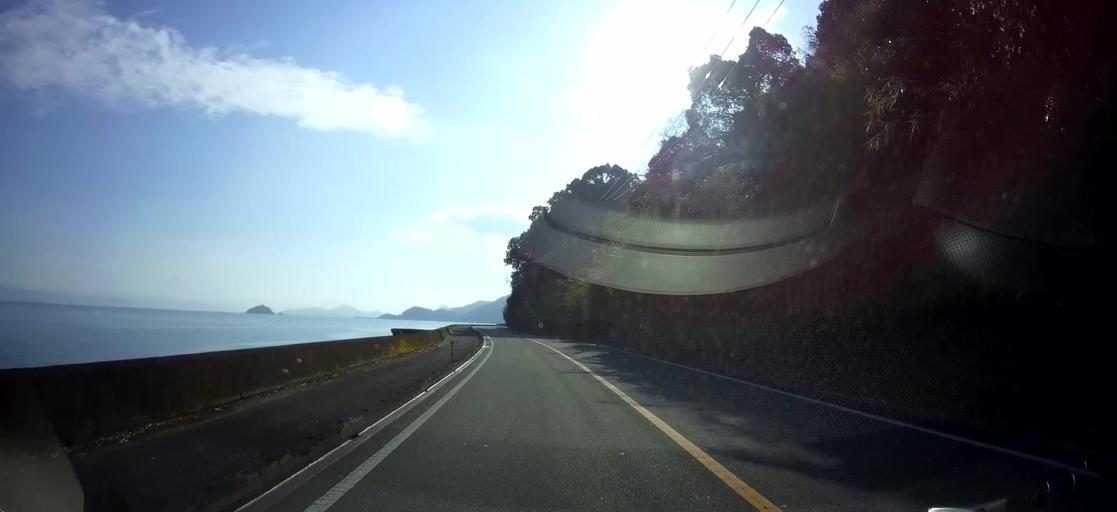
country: JP
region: Kumamoto
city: Yatsushiro
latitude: 32.4985
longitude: 130.4462
